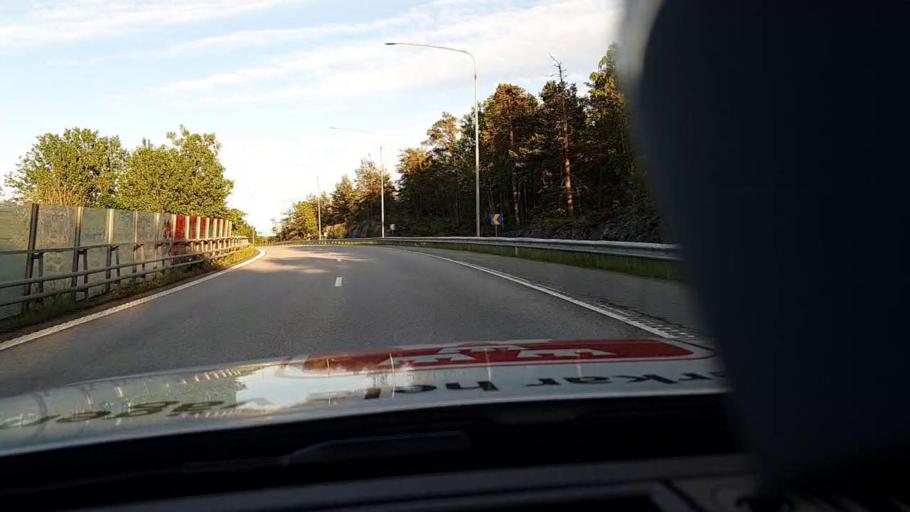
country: SE
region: Stockholm
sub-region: Nacka Kommun
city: Alta
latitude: 59.2461
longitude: 18.1786
